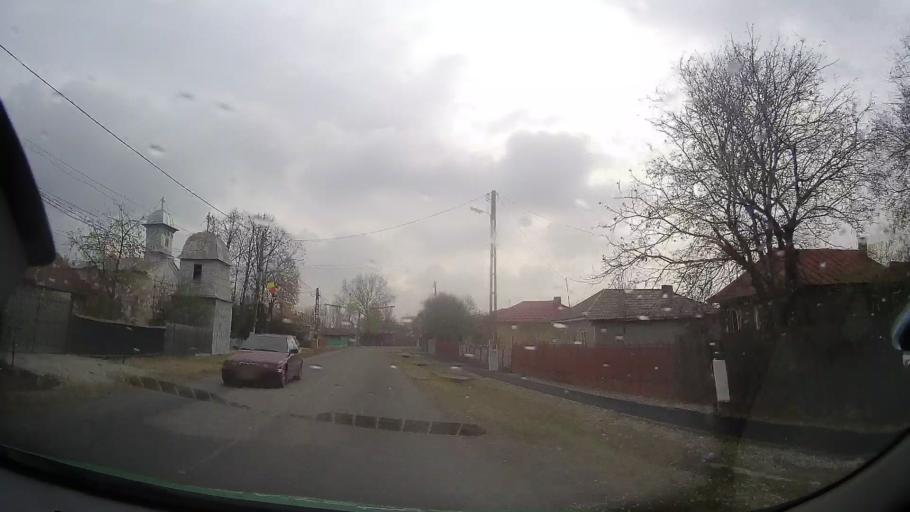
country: RO
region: Prahova
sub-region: Comuna Draganesti
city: Draganesti
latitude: 44.8412
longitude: 26.2692
